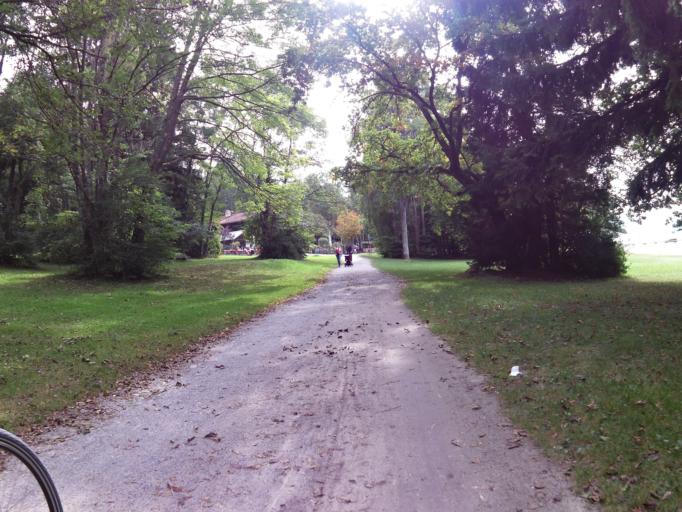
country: DE
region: Bavaria
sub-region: Upper Bavaria
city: Seeshaupt
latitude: 47.8460
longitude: 11.3386
